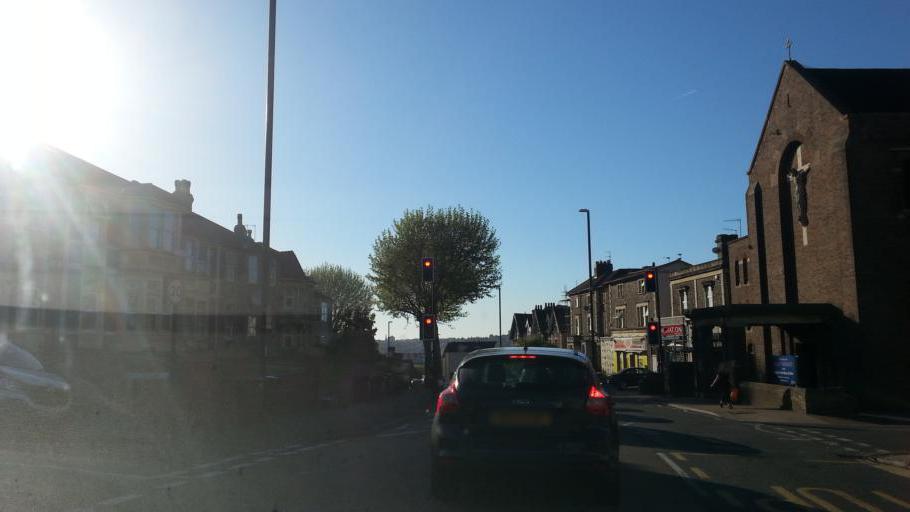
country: GB
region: England
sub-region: Bristol
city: Bristol
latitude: 51.4401
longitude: -2.5739
